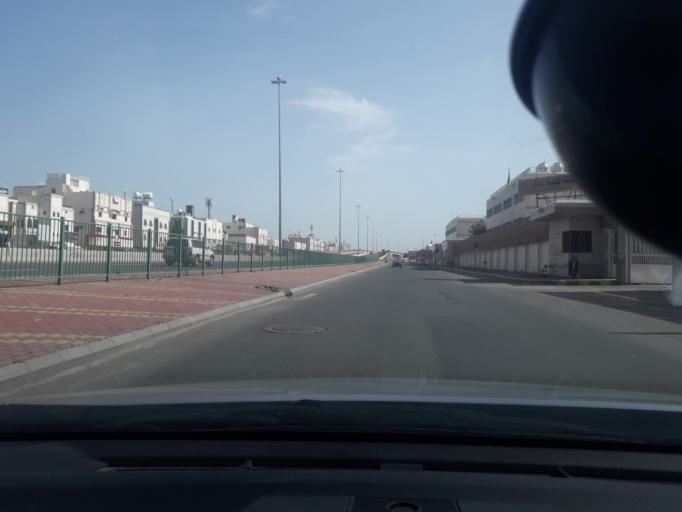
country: SA
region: Al Madinah al Munawwarah
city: Medina
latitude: 24.4486
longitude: 39.6600
